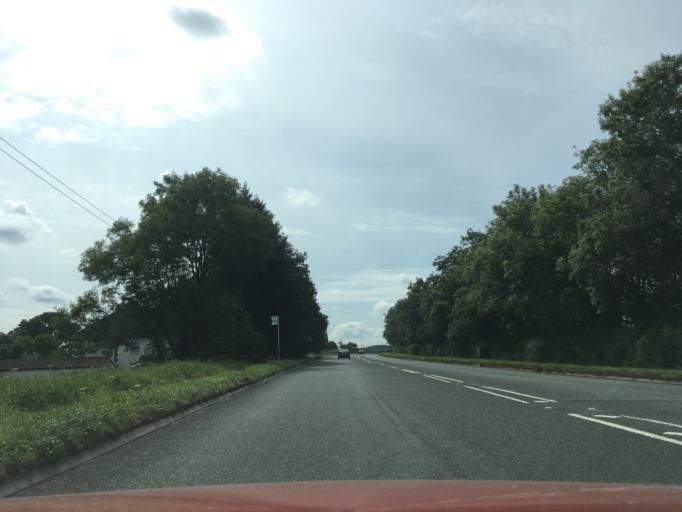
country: GB
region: England
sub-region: South Gloucestershire
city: Falfield
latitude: 51.6302
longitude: -2.4619
